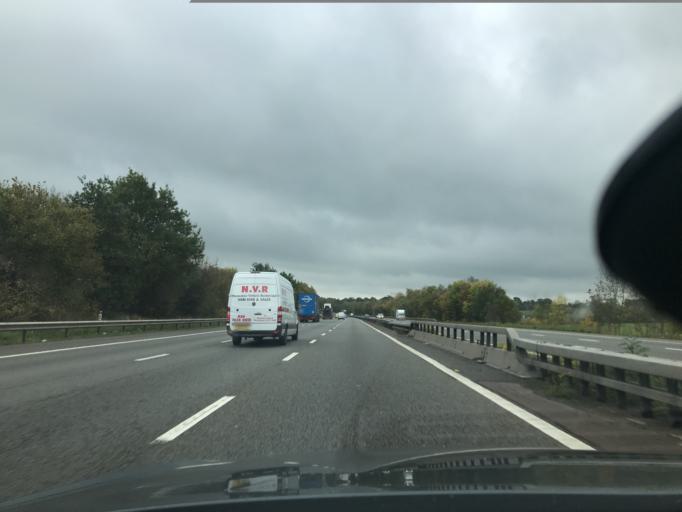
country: GB
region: England
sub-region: Warwickshire
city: Wroxall
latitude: 52.3144
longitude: -1.7142
